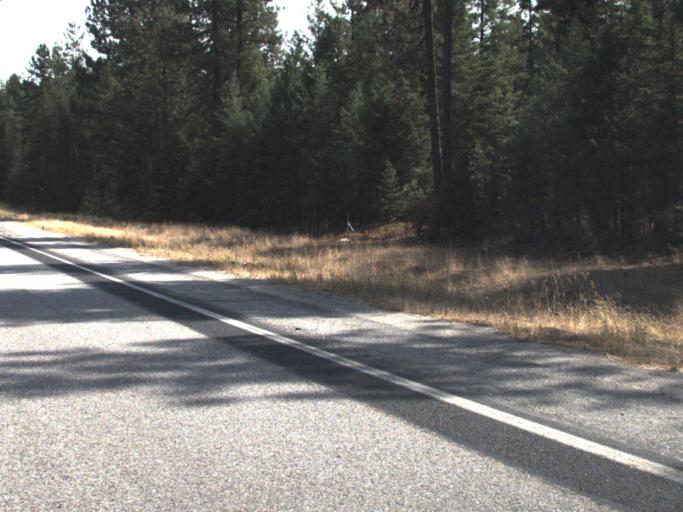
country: US
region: Washington
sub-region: Stevens County
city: Chewelah
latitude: 48.1443
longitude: -117.6706
